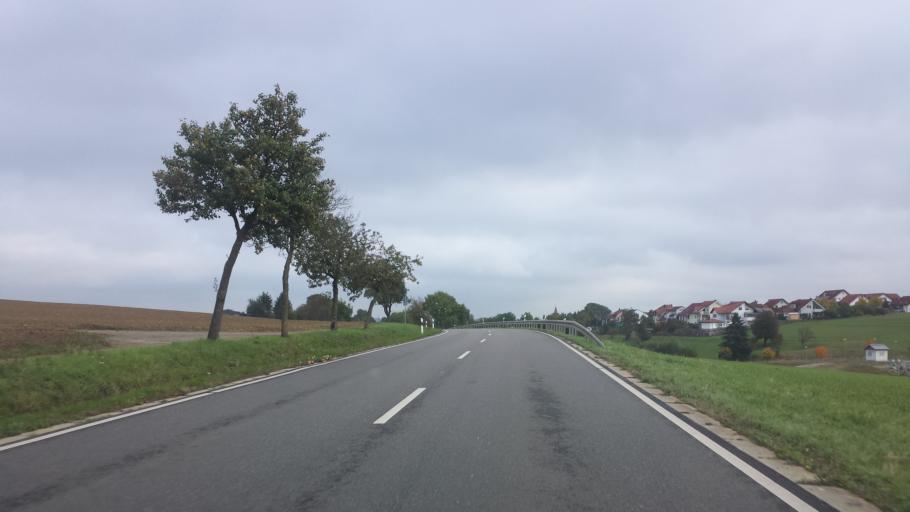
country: DE
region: Baden-Wuerttemberg
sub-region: Regierungsbezirk Stuttgart
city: Massenbachhausen
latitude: 49.2087
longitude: 9.0468
